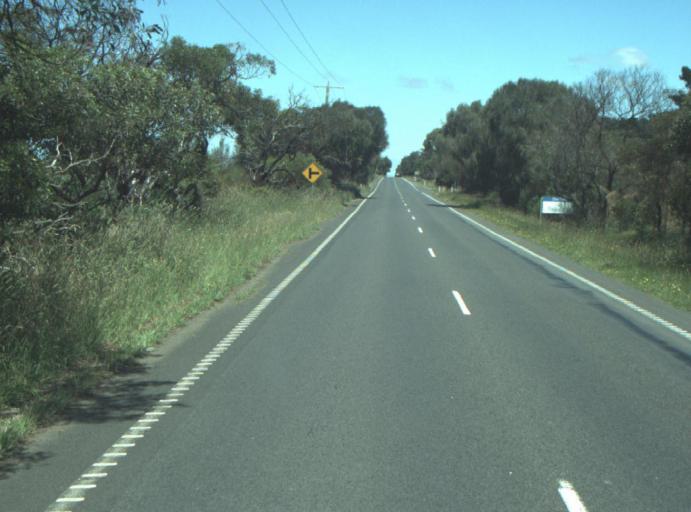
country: AU
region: Victoria
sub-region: Queenscliffe
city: Queenscliff
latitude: -38.1798
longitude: 144.6961
